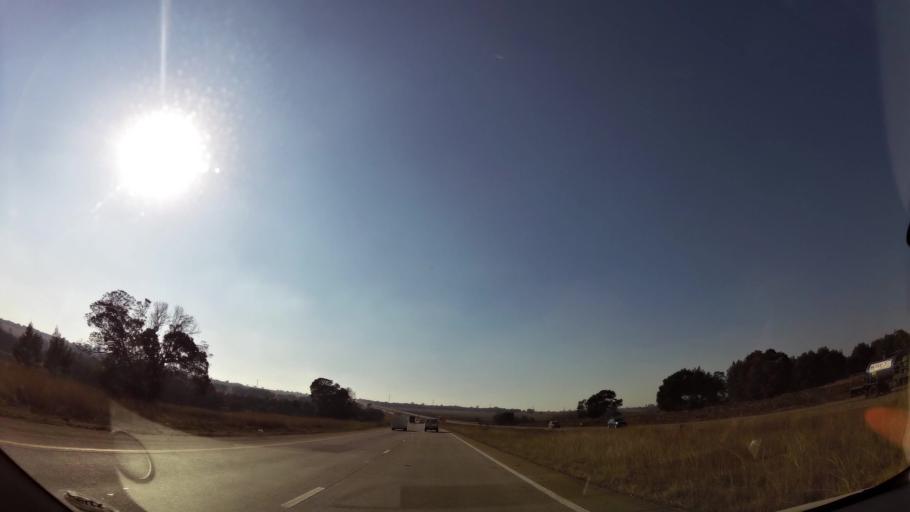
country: ZA
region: Mpumalanga
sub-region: Nkangala District Municipality
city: Witbank
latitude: -26.0225
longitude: 29.0494
